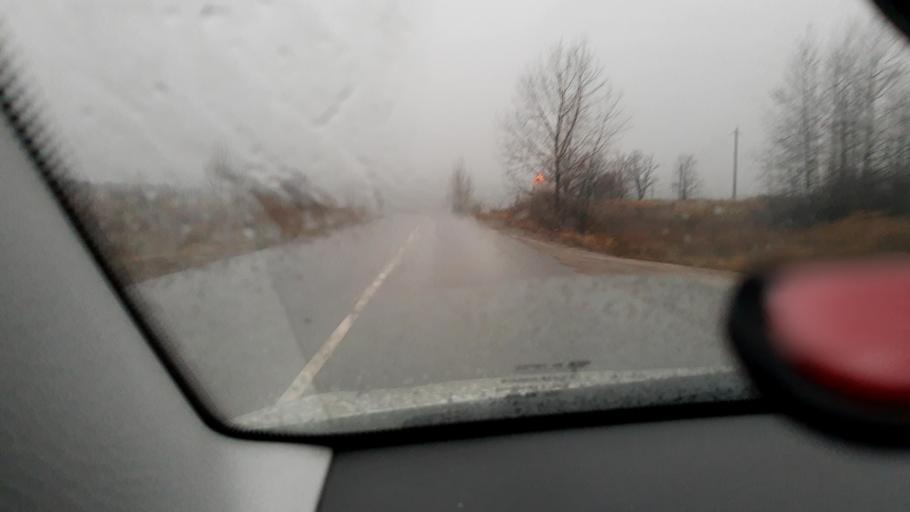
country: RU
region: Bashkortostan
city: Iglino
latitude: 54.8994
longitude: 56.2210
